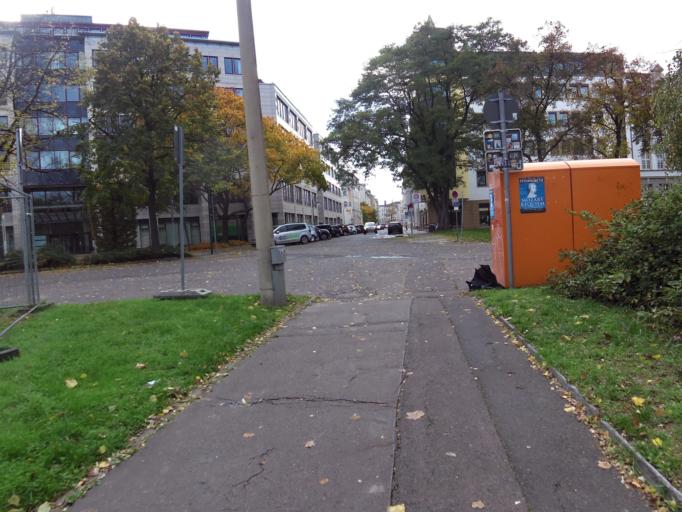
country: DE
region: Saxony
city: Leipzig
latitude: 51.3424
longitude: 12.3691
